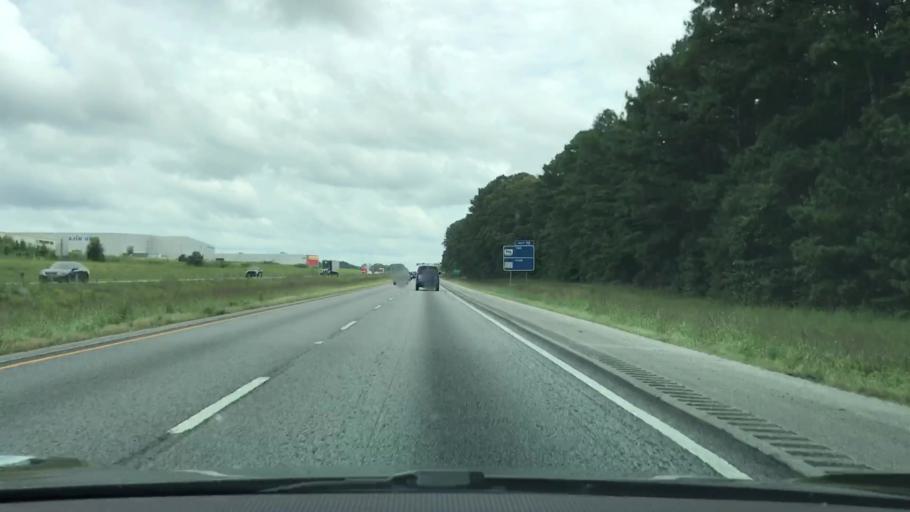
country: US
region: Alabama
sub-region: Chambers County
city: Huguley
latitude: 32.7367
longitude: -85.2885
